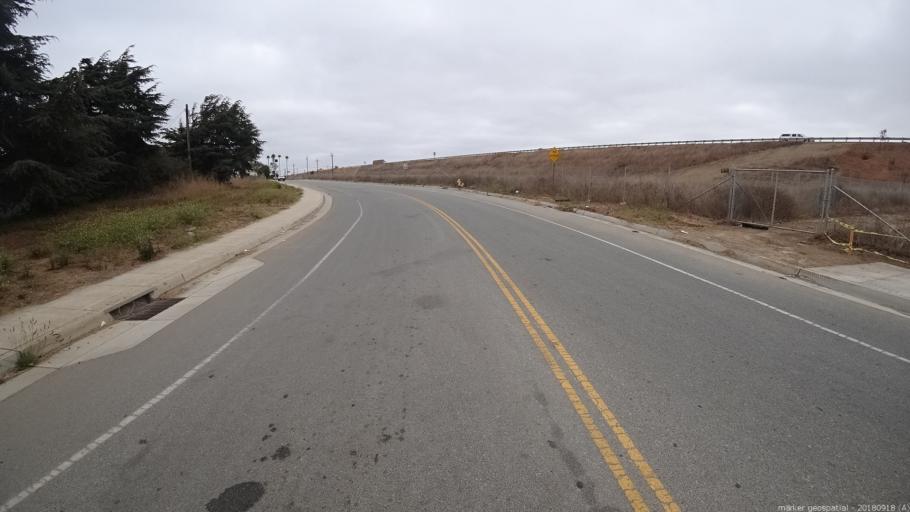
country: US
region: California
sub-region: Monterey County
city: Boronda
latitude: 36.7353
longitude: -121.6582
